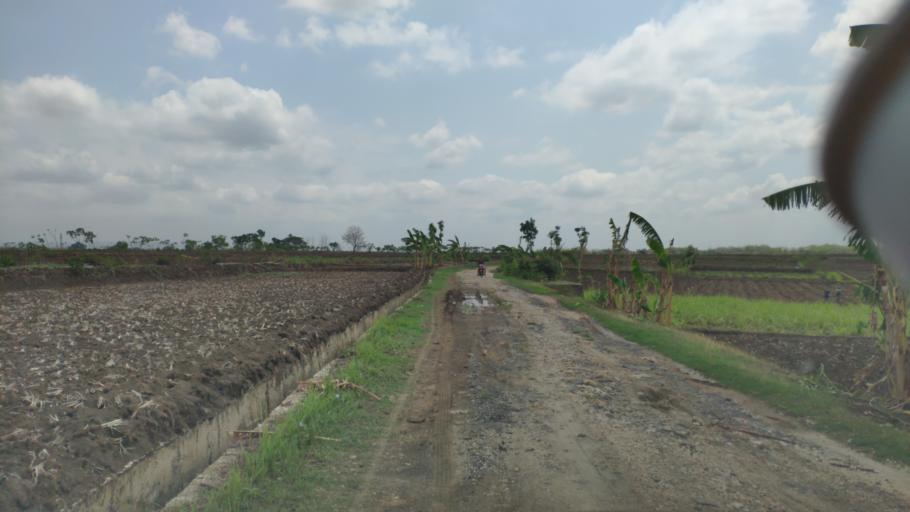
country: ID
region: Central Java
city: Gumiring
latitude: -7.0287
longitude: 111.3787
